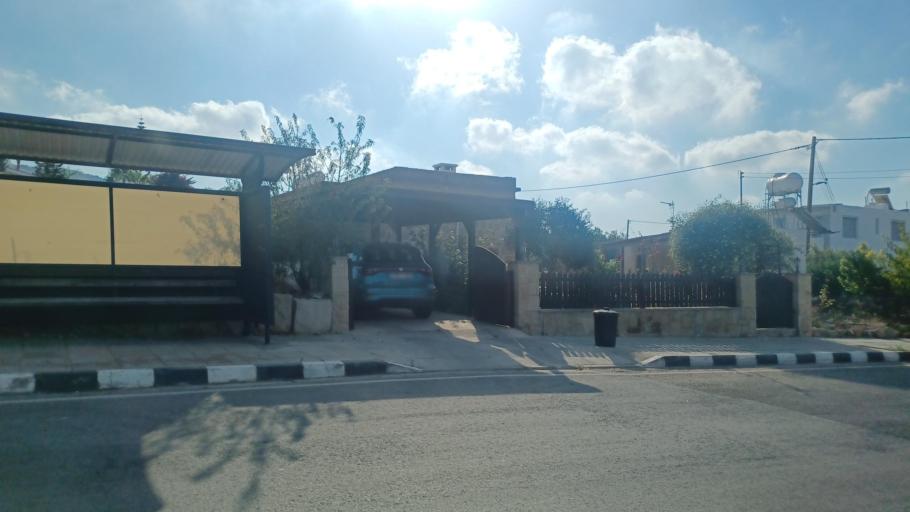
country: CY
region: Pafos
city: Mesogi
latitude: 34.7886
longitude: 32.4608
